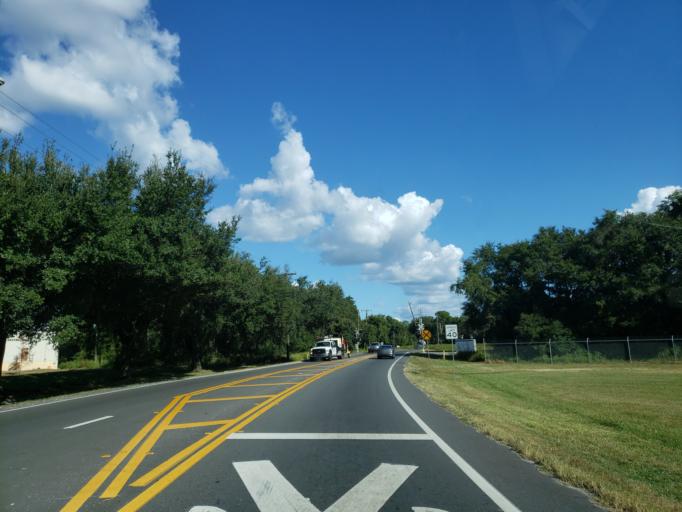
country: US
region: Florida
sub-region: Hillsborough County
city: Plant City
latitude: 28.0044
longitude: -82.1440
